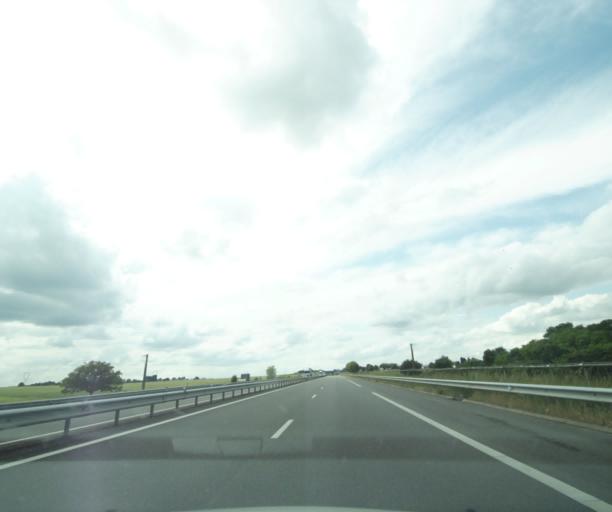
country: FR
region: Centre
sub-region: Departement du Cher
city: Trouy
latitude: 47.0403
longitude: 2.3518
